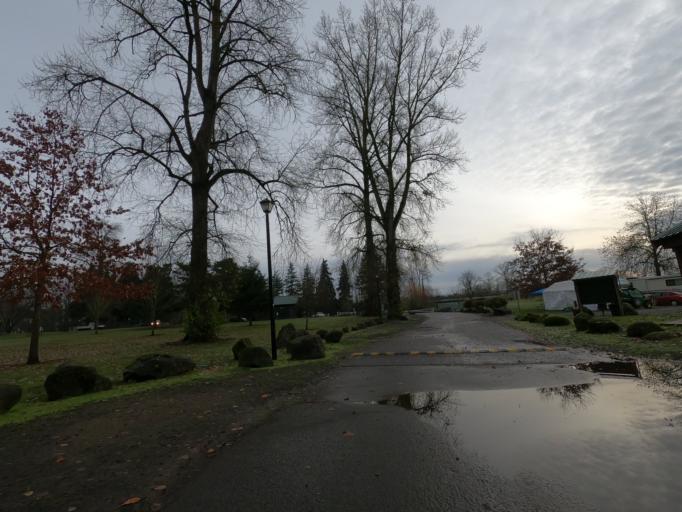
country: US
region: Oregon
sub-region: Clackamas County
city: West Linn
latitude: 45.3705
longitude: -122.6036
